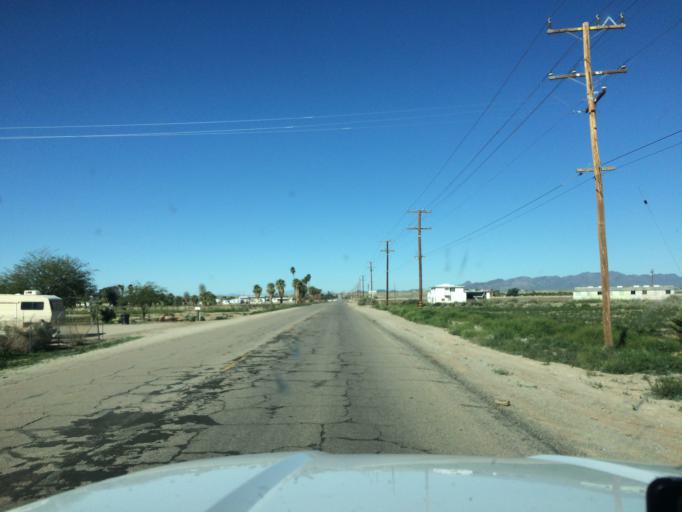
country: US
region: California
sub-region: Riverside County
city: Blythe
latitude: 33.6101
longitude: -114.6423
